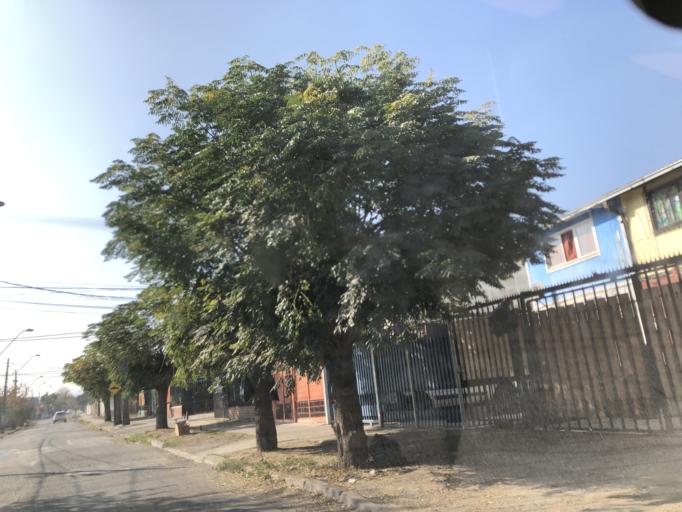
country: CL
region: Santiago Metropolitan
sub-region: Provincia de Cordillera
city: Puente Alto
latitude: -33.6210
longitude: -70.5939
